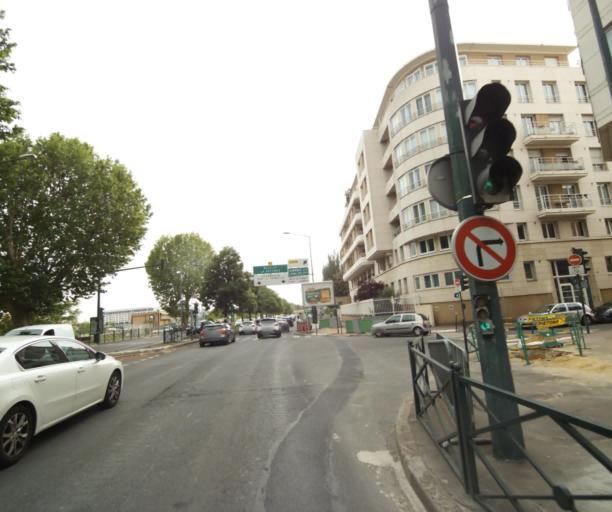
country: FR
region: Ile-de-France
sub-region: Departement des Hauts-de-Seine
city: Asnieres-sur-Seine
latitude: 48.9070
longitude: 2.2910
